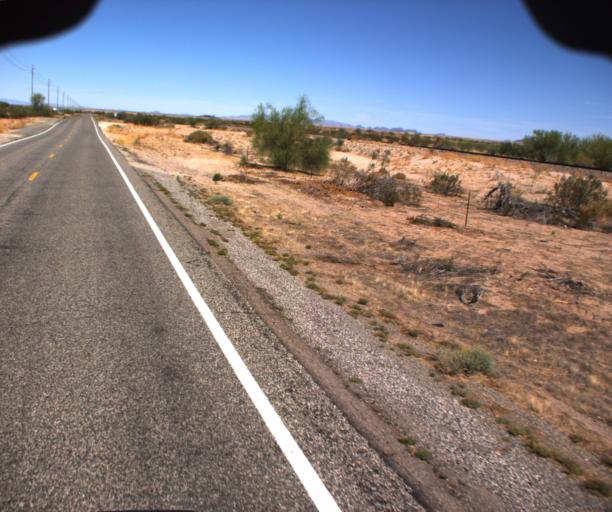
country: US
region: Arizona
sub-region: La Paz County
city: Cienega Springs
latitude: 33.9758
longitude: -114.0492
